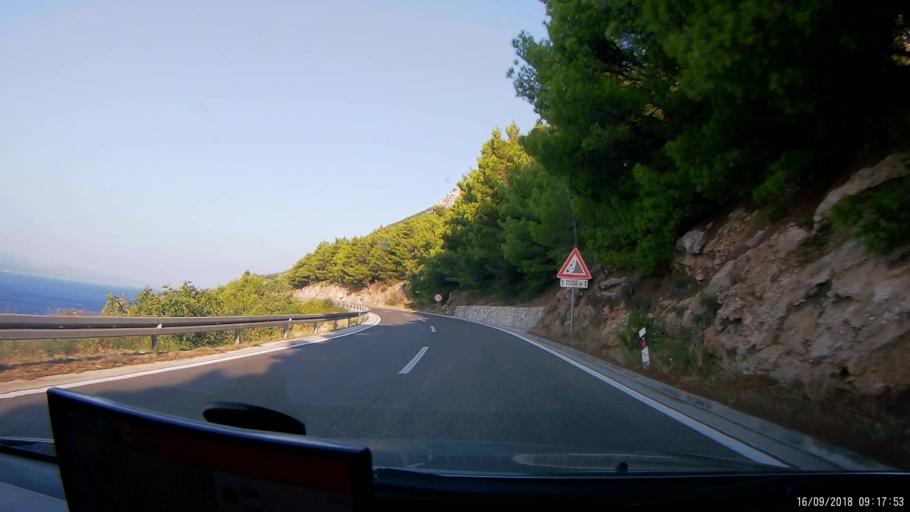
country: HR
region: Splitsko-Dalmatinska
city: Donja Brela
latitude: 43.4030
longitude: 16.8505
